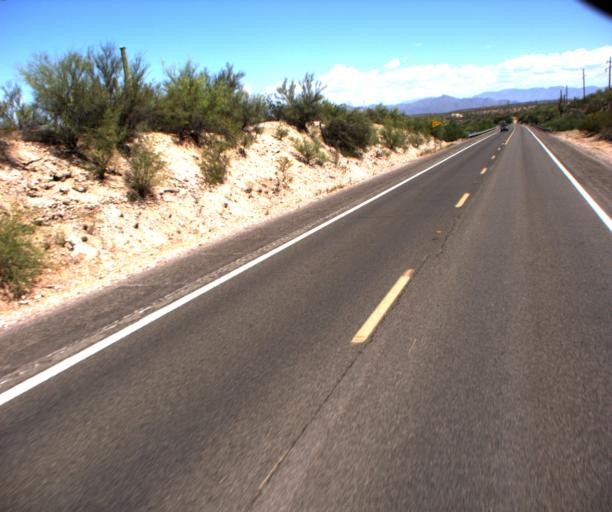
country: US
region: Arizona
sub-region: Pinal County
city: Mammoth
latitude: 32.9068
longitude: -110.7179
